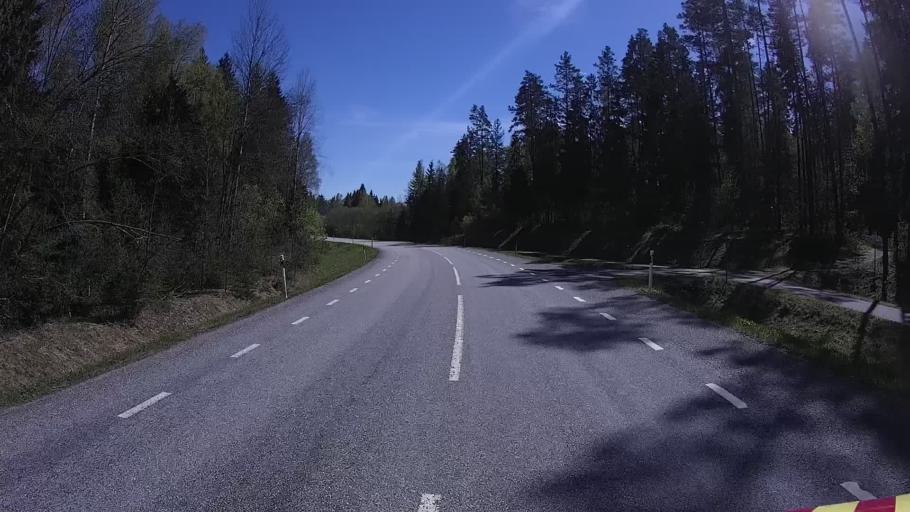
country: EE
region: Harju
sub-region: Kuusalu vald
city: Kuusalu
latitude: 59.2636
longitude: 25.6555
